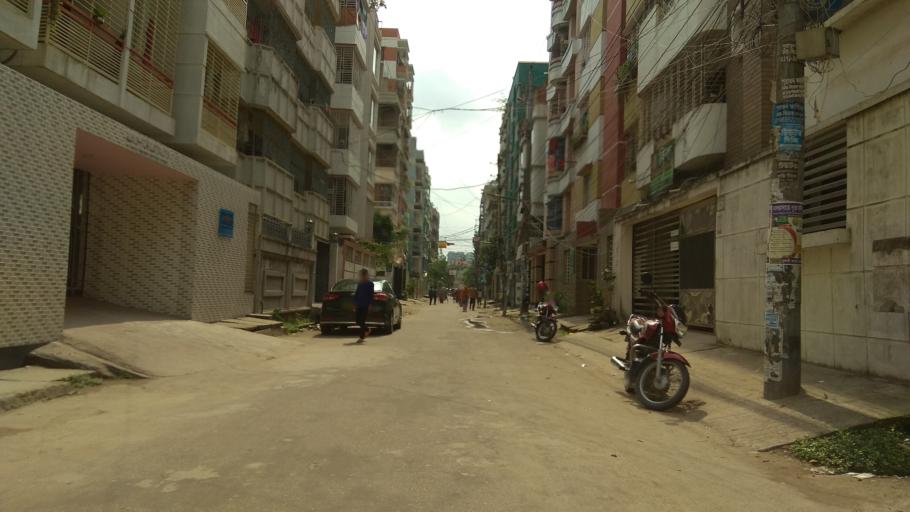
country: BD
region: Dhaka
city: Azimpur
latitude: 23.8140
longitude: 90.3540
